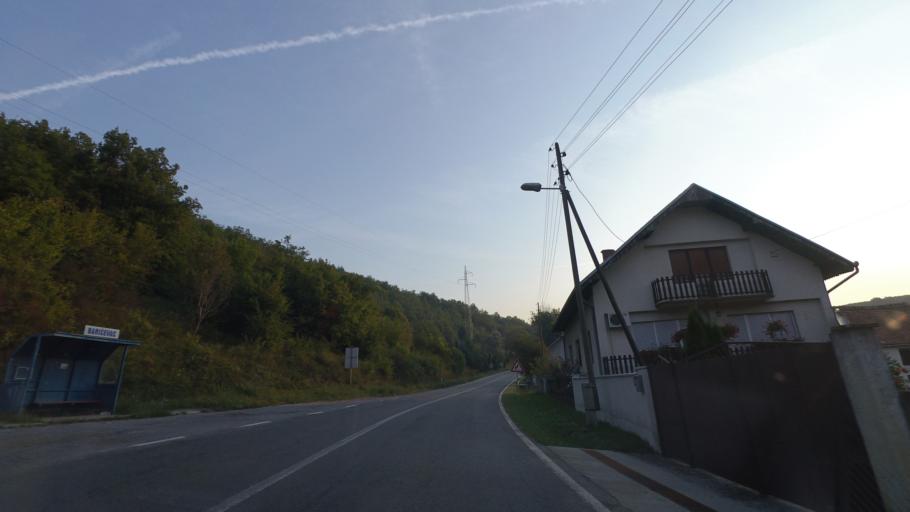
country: HR
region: Brodsko-Posavska
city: Resetari
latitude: 45.3383
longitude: 17.4562
